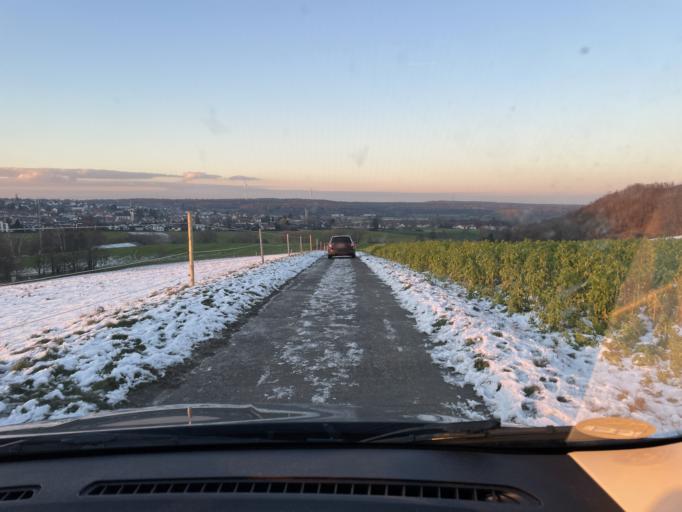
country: DE
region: Hesse
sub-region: Regierungsbezirk Darmstadt
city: Rossdorf
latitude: 49.8491
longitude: 8.7650
